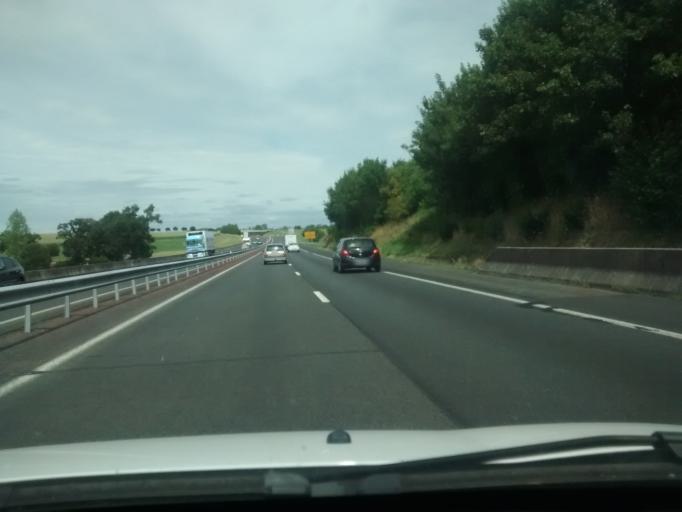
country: FR
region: Lower Normandy
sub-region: Departement de la Manche
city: Saint-Quentin-sur-le-Homme
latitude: 48.6121
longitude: -1.3348
